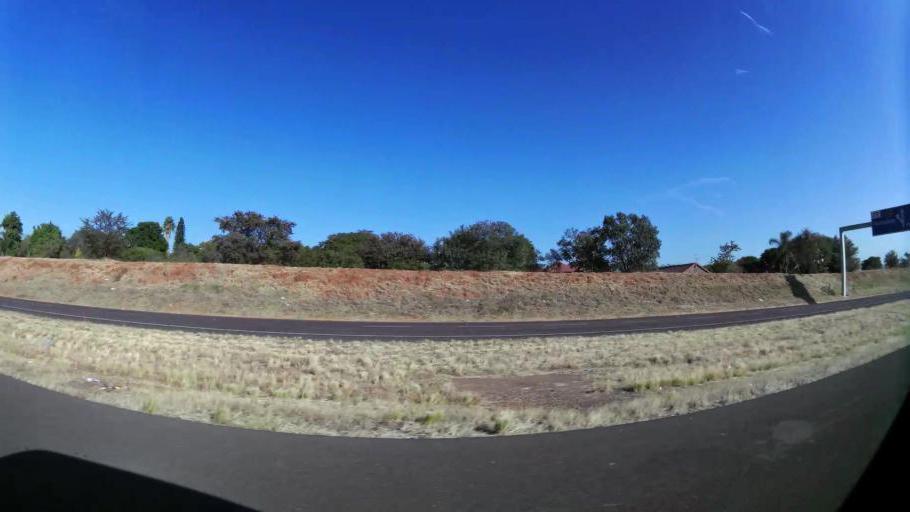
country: ZA
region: Gauteng
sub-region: City of Tshwane Metropolitan Municipality
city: Pretoria
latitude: -25.6601
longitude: 28.1143
